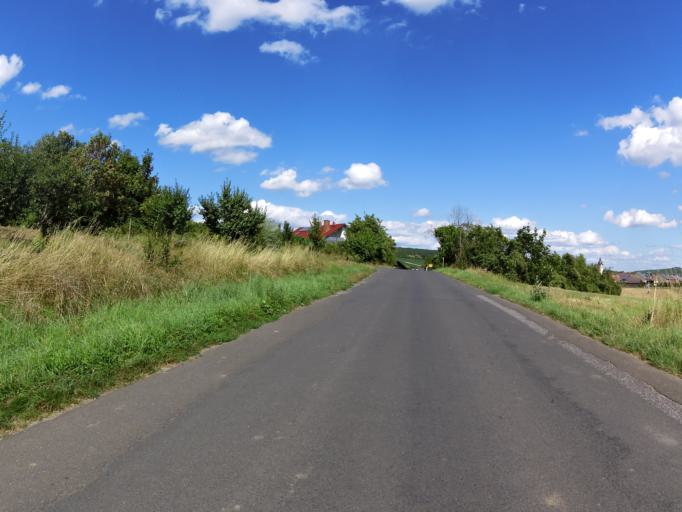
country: DE
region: Bavaria
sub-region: Regierungsbezirk Unterfranken
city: Prosselsheim
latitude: 49.8792
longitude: 10.1534
